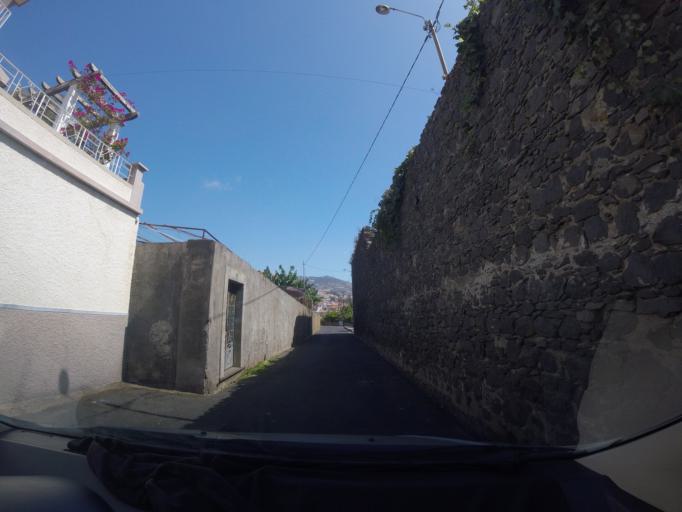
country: PT
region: Madeira
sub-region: Funchal
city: Nossa Senhora do Monte
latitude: 32.6542
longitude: -16.9079
